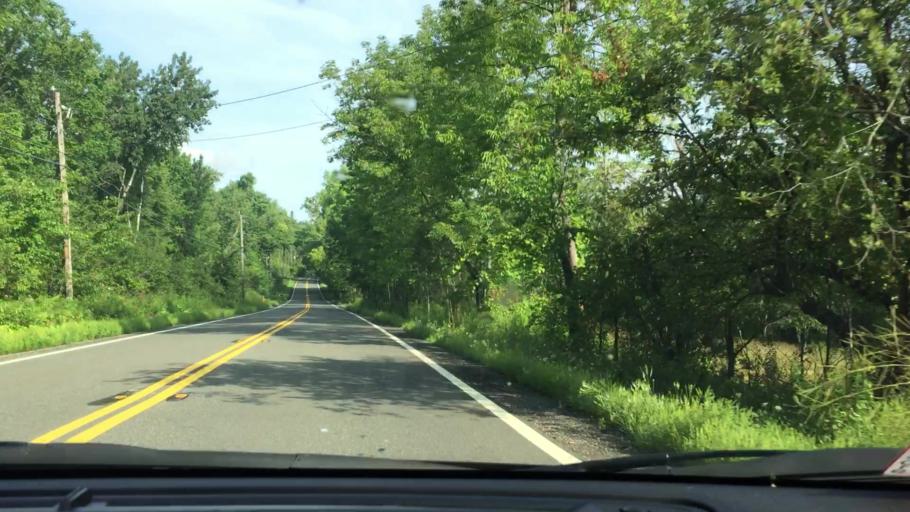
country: US
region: Massachusetts
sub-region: Berkshire County
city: Becket
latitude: 42.3396
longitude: -73.1110
